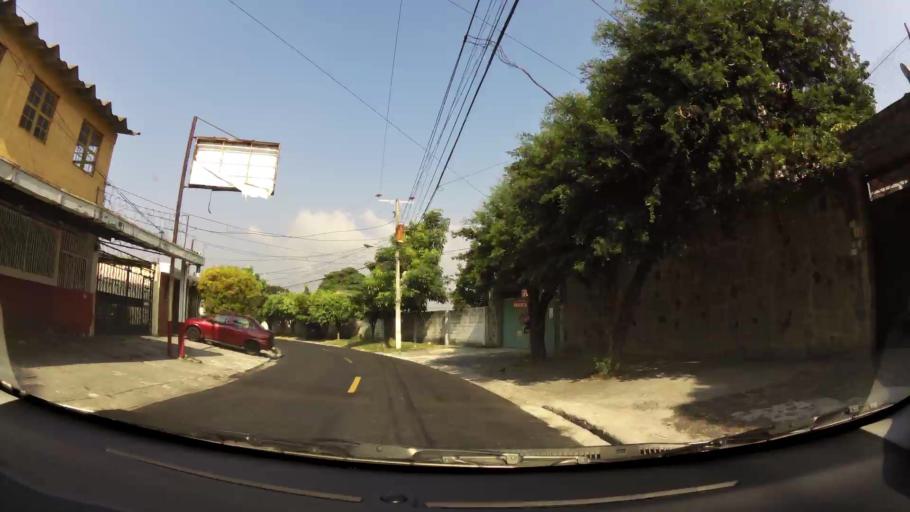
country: SV
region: La Libertad
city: Antiguo Cuscatlan
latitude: 13.6748
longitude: -89.2351
